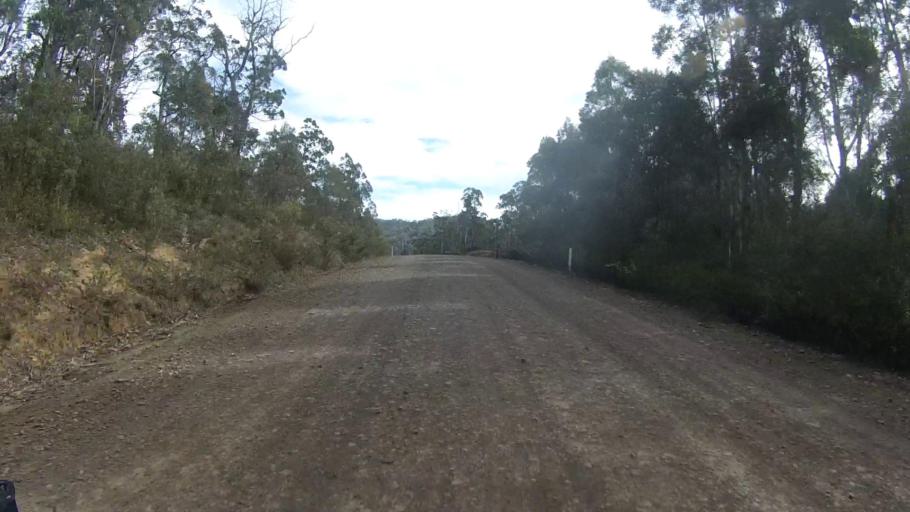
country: AU
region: Tasmania
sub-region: Sorell
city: Sorell
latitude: -42.7590
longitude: 147.8293
